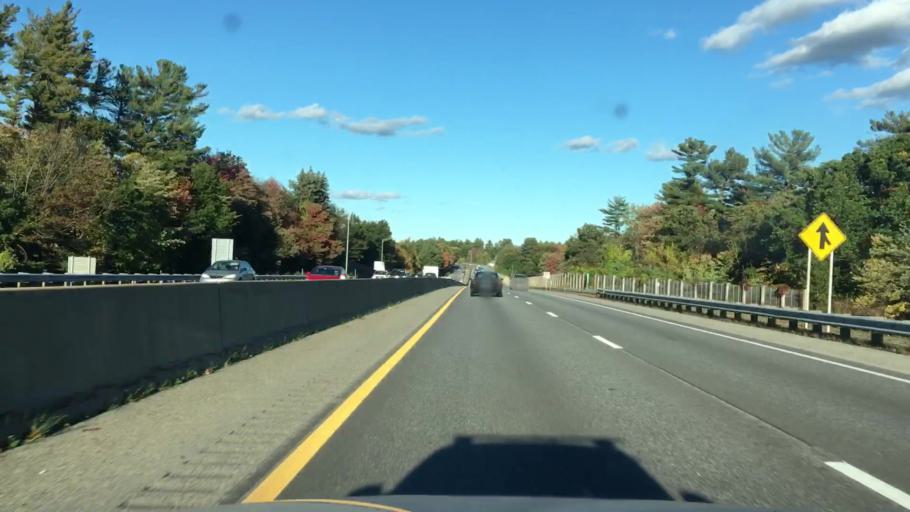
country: US
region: New Hampshire
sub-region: Rockingham County
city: Auburn
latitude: 43.0070
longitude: -71.3937
